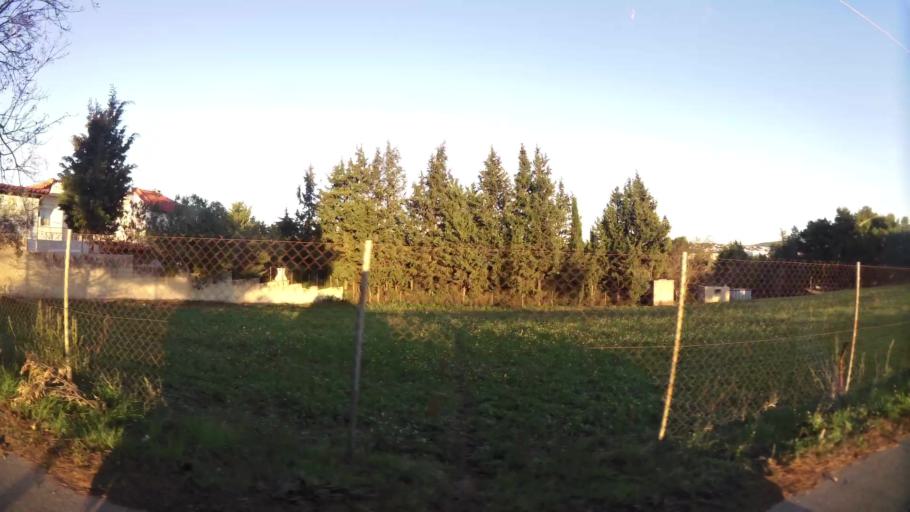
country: GR
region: Attica
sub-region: Nomarchia Anatolikis Attikis
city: Agios Stefanos
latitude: 38.1463
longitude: 23.8420
